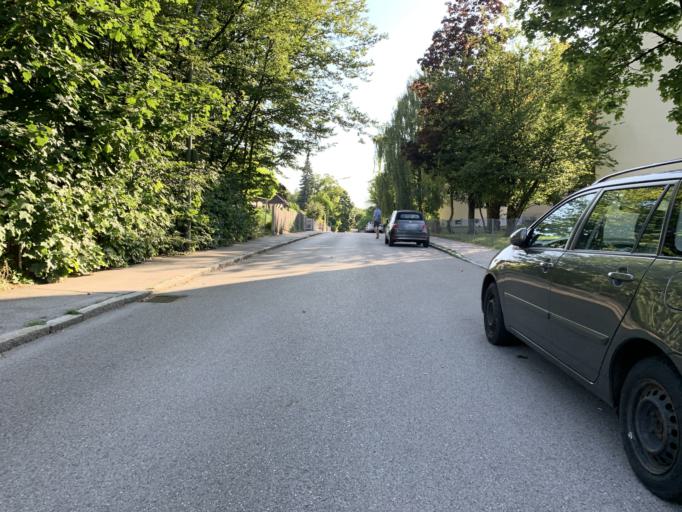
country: DE
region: Bavaria
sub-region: Upper Bavaria
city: Freising
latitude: 48.4073
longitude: 11.7543
